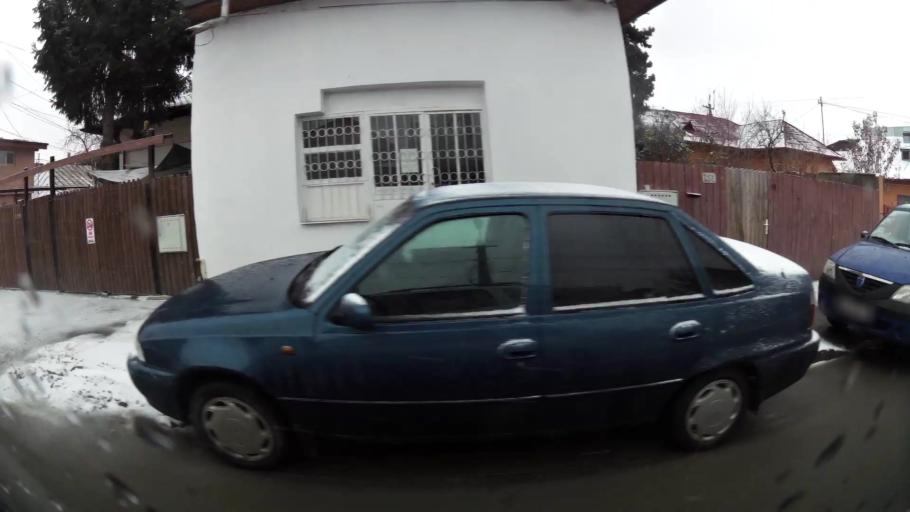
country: RO
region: Prahova
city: Ploiesti
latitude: 44.9272
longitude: 26.0167
